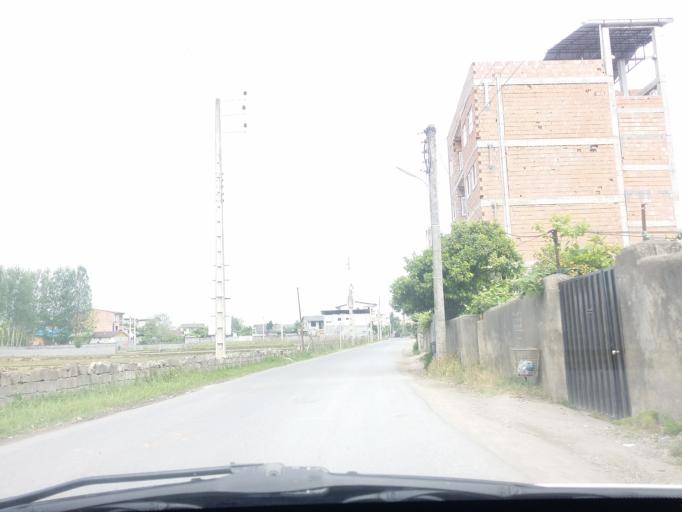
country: IR
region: Mazandaran
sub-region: Nowshahr
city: Nowshahr
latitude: 36.6254
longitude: 51.4905
